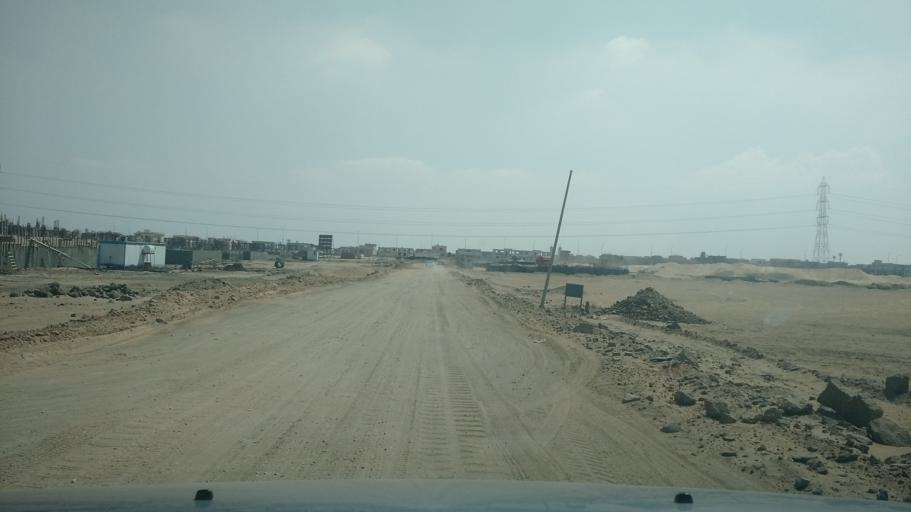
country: EG
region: Al Jizah
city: Awsim
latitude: 30.0255
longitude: 30.9622
